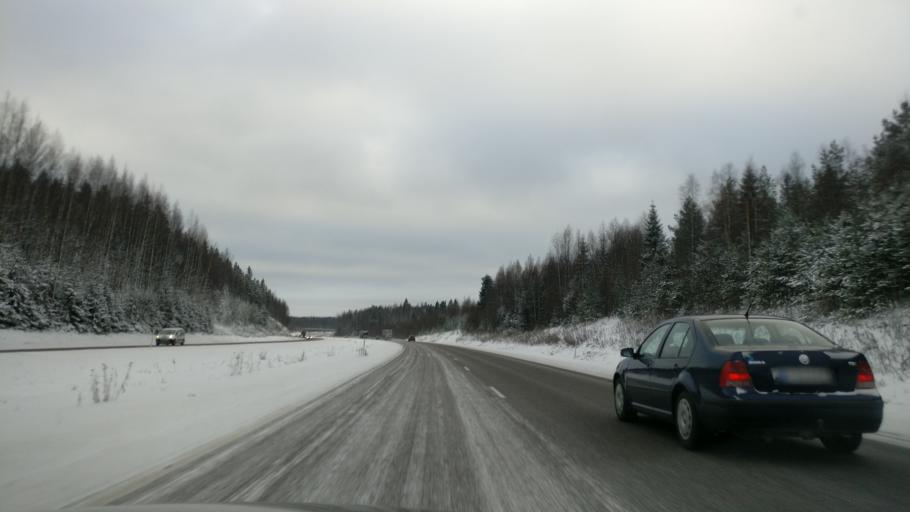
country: FI
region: Paijanne Tavastia
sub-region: Lahti
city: Nastola
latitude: 61.0265
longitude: 25.8321
